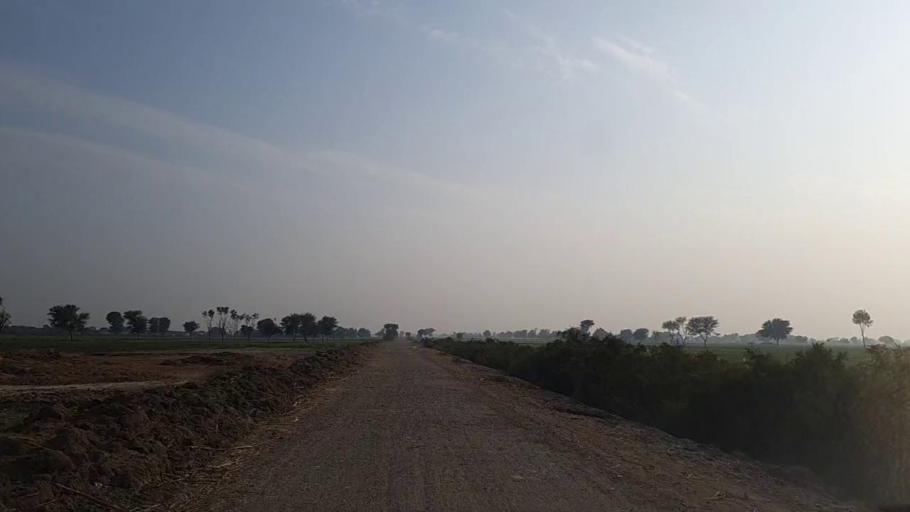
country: PK
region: Sindh
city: Jam Sahib
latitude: 26.3164
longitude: 68.5336
